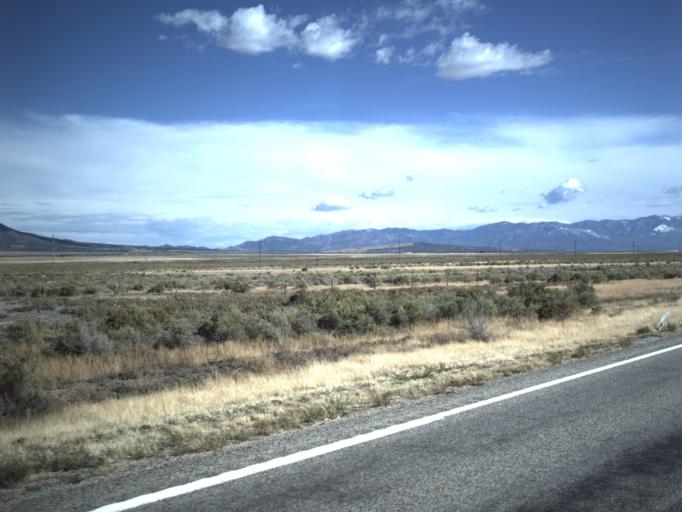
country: US
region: Utah
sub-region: Millard County
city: Delta
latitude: 39.2587
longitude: -112.4448
